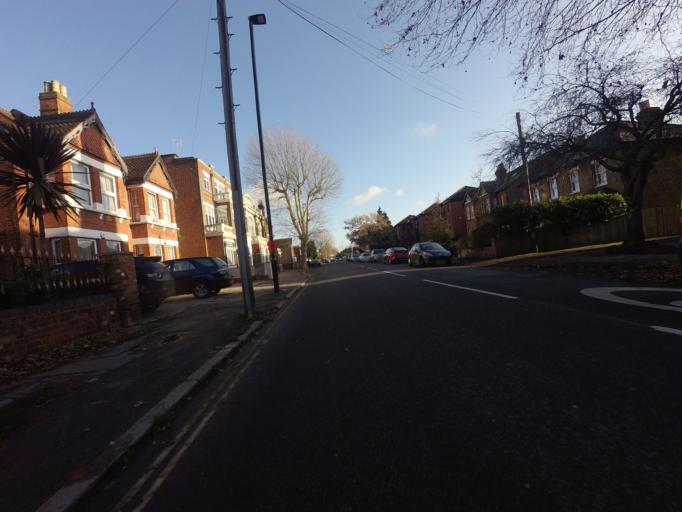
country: GB
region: England
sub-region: Greater London
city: Feltham
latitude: 51.4474
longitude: -0.4061
